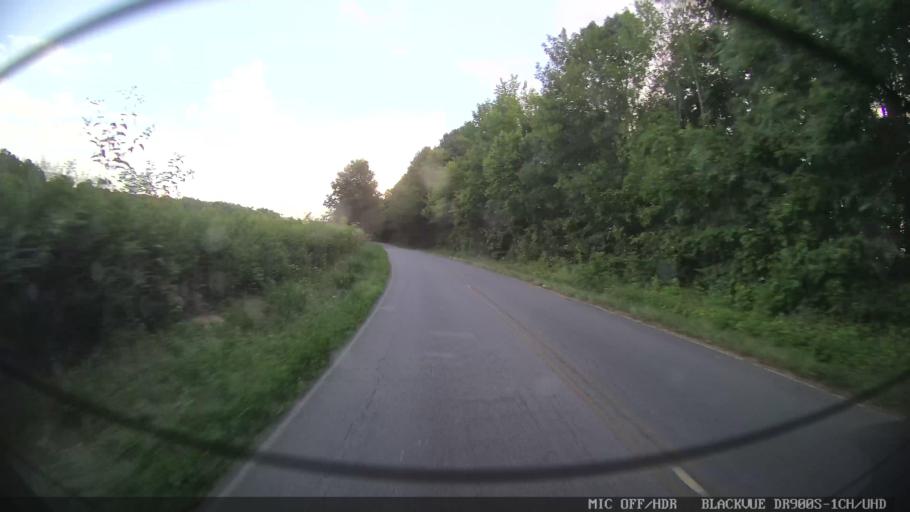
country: US
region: Georgia
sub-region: Bartow County
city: Rydal
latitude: 34.2766
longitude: -84.7997
